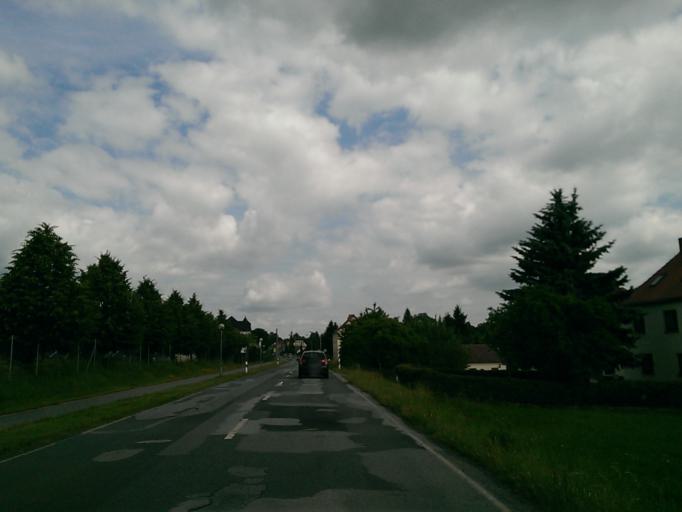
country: DE
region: Saxony
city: Mittelherwigsdorf
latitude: 50.9441
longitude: 14.7401
